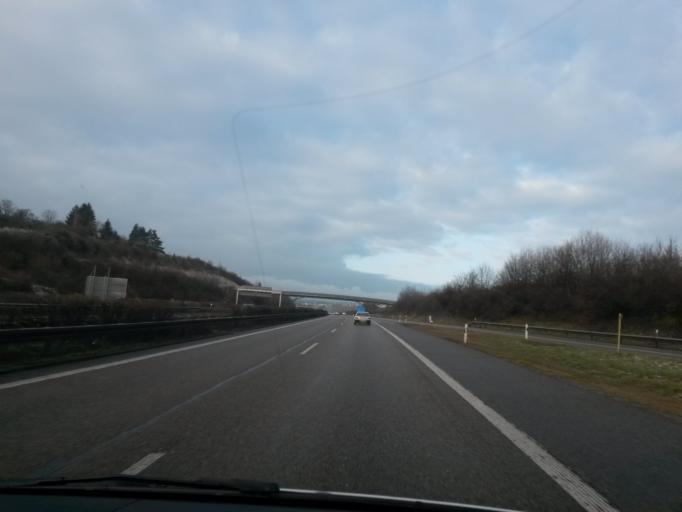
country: DE
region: Baden-Wuerttemberg
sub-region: Regierungsbezirk Stuttgart
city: Leonberg
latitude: 48.7829
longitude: 9.0080
